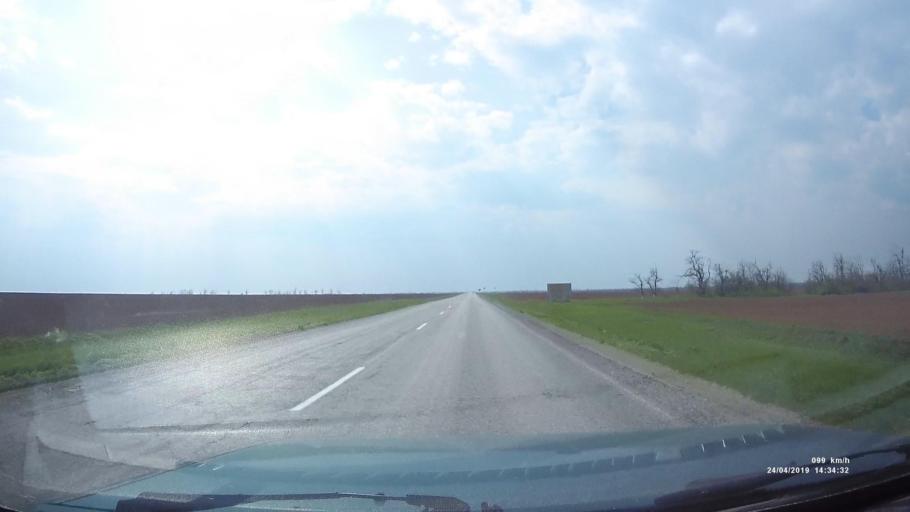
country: RU
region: Kalmykiya
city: Arshan'
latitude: 46.3737
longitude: 43.9305
